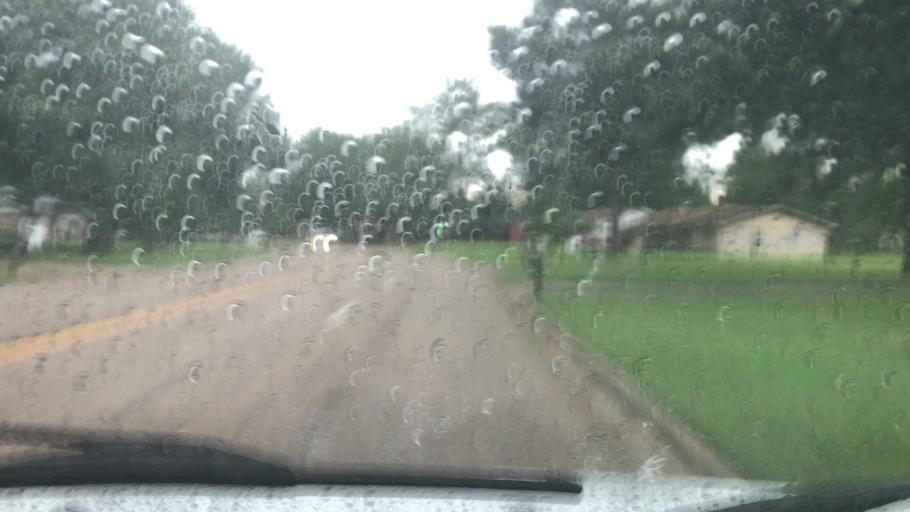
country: US
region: Texas
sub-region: Bowie County
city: Wake Village
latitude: 33.4036
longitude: -94.0798
